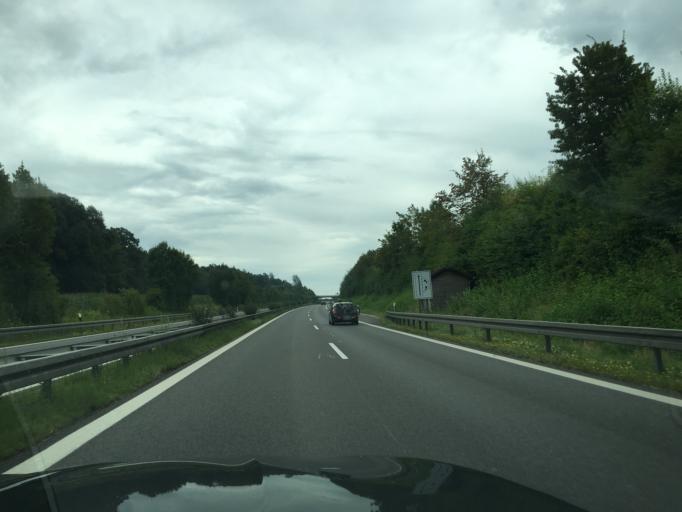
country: DE
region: Baden-Wuerttemberg
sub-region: Freiburg Region
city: Radolfzell am Bodensee
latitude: 47.7454
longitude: 9.0130
